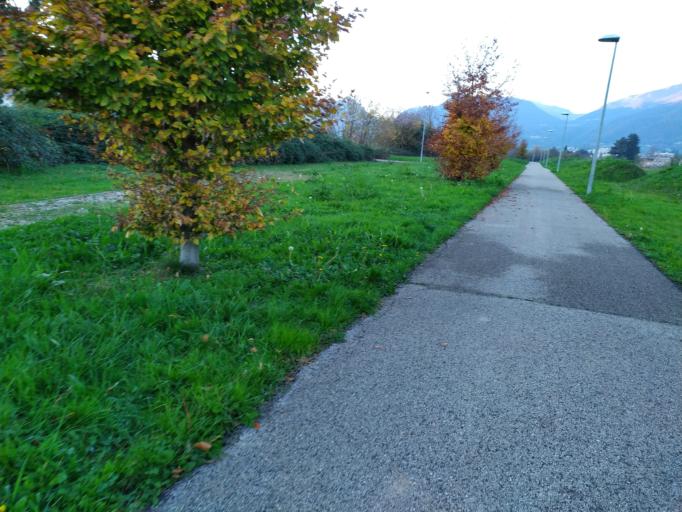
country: IT
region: Veneto
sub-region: Provincia di Vicenza
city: Schio
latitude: 45.7044
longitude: 11.3665
